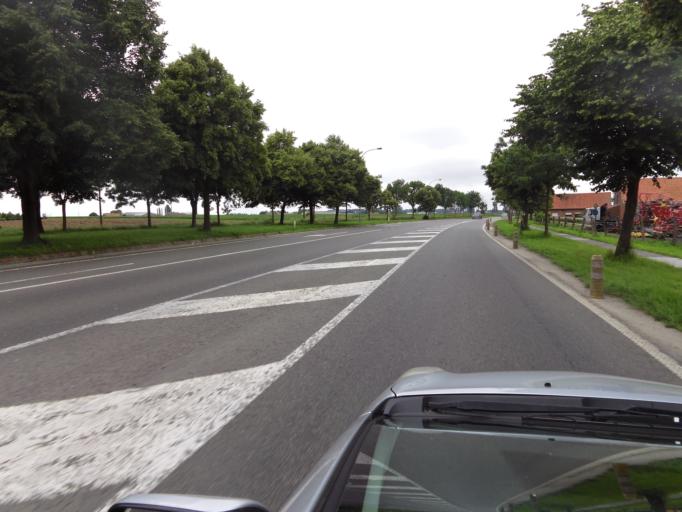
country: BE
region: Flanders
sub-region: Provincie West-Vlaanderen
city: Ieper
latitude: 50.9025
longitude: 2.8497
